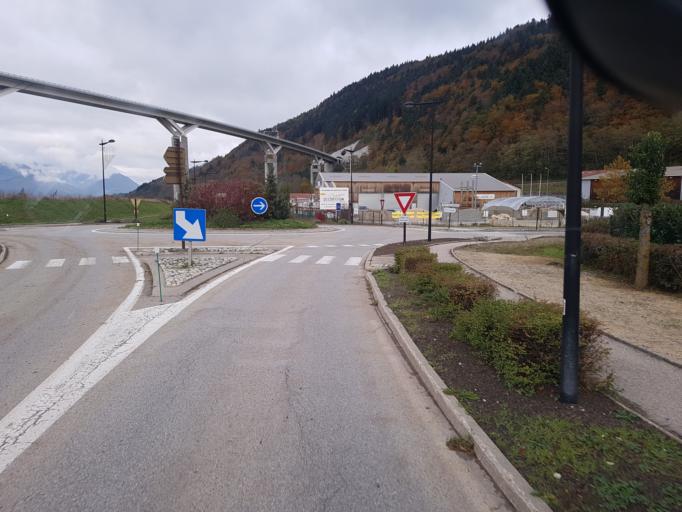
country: FR
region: Rhone-Alpes
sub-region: Departement de l'Isere
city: La Motte-Saint-Martin
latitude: 44.9289
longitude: 5.6393
